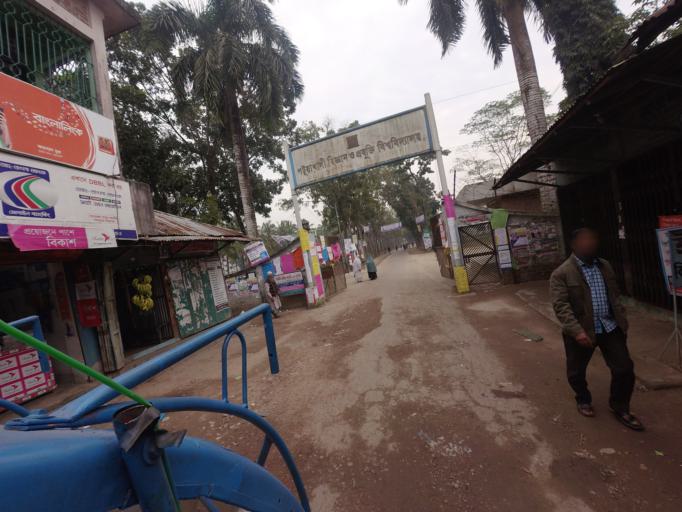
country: BD
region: Barisal
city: Nalchiti
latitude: 22.4643
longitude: 90.3808
